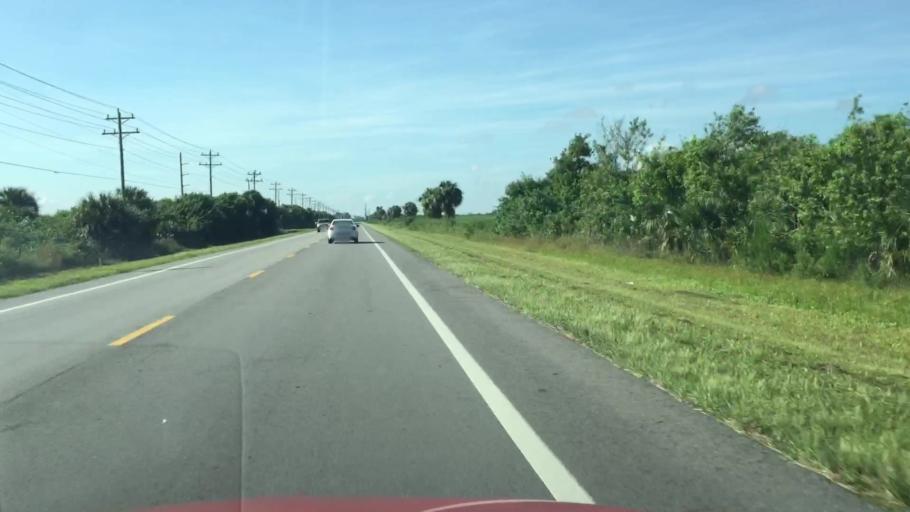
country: US
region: Florida
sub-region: Collier County
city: Immokalee
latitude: 26.3839
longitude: -81.4171
